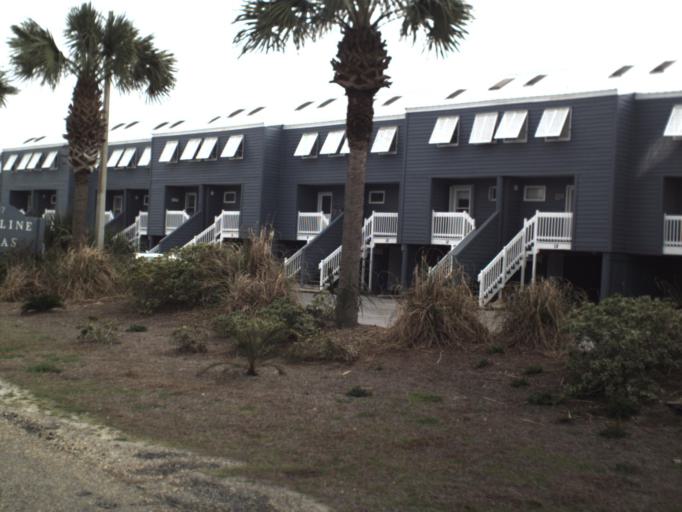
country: US
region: Florida
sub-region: Bay County
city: Laguna Beach
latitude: 30.2606
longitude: -85.9729
